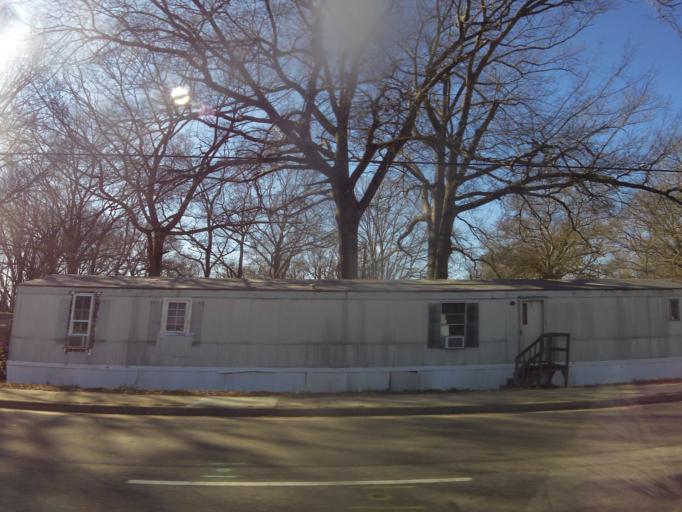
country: US
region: Virginia
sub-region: City of Newport News
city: Newport News
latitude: 36.9991
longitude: -76.4321
